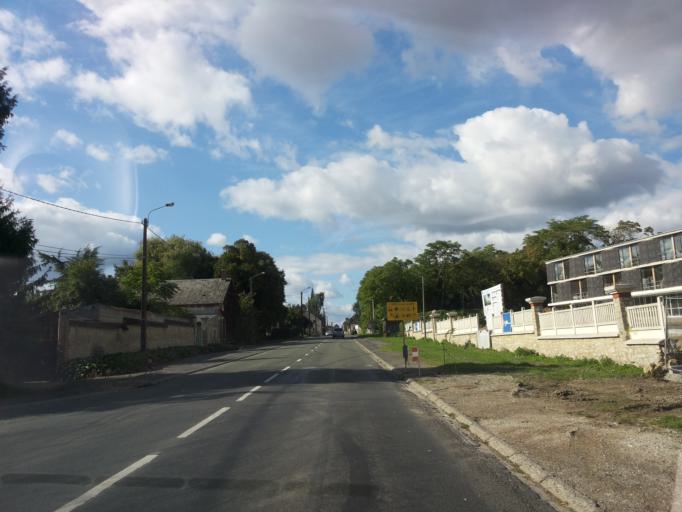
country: FR
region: Picardie
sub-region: Departement de l'Aisne
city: Saint-Erme-Outre-et-Ramecourt
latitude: 49.4592
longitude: 3.8284
